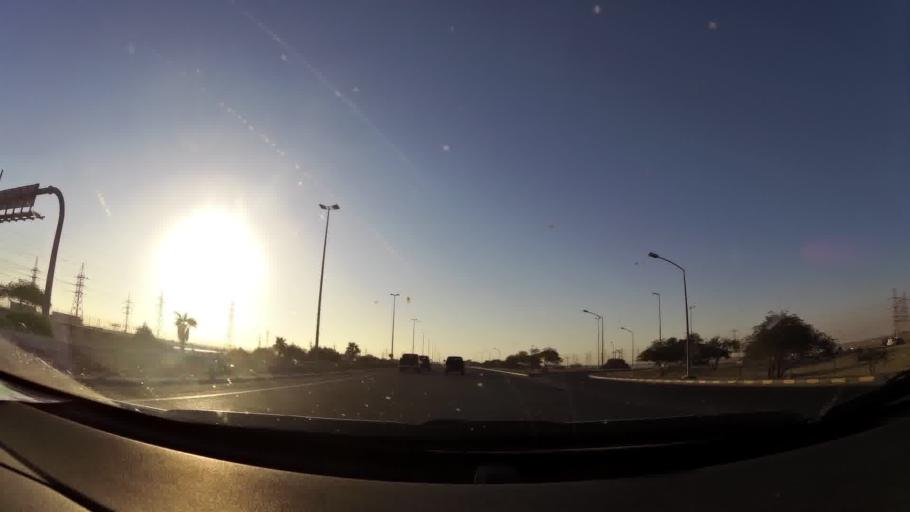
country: KW
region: Al Ahmadi
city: Al Fahahil
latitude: 28.8796
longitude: 48.2294
